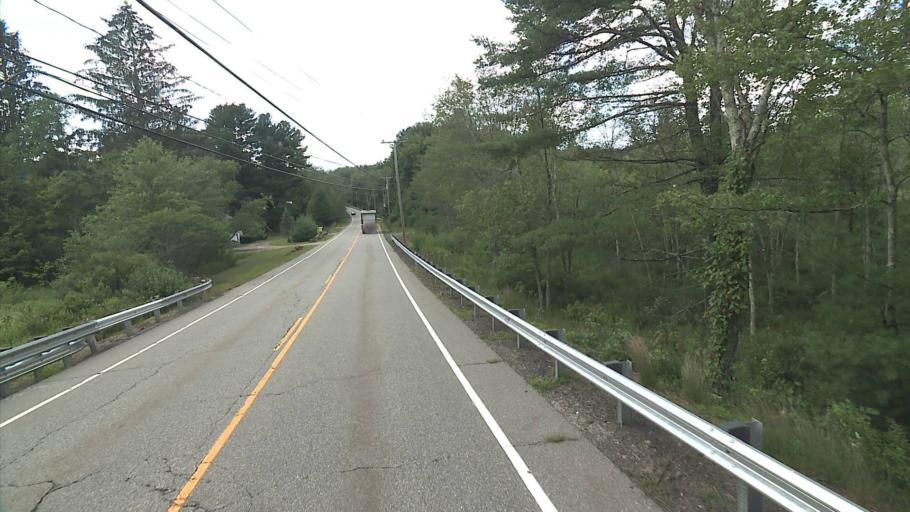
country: US
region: Connecticut
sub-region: Tolland County
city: Stafford
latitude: 41.9632
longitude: -72.2450
